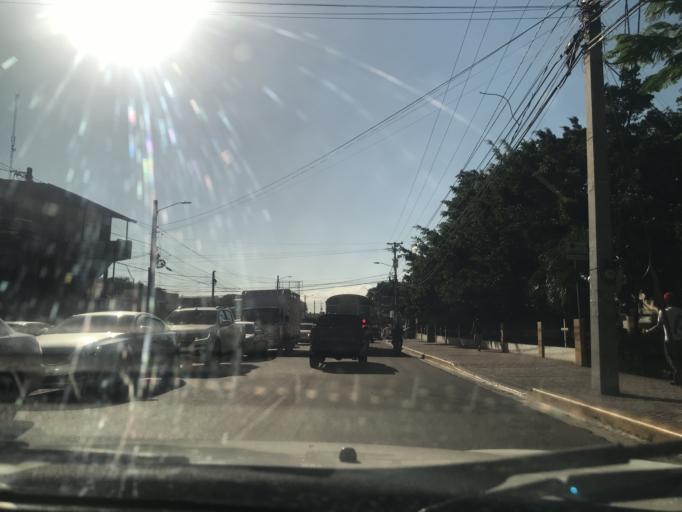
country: DO
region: Santiago
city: Santiago de los Caballeros
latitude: 19.4328
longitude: -70.6947
